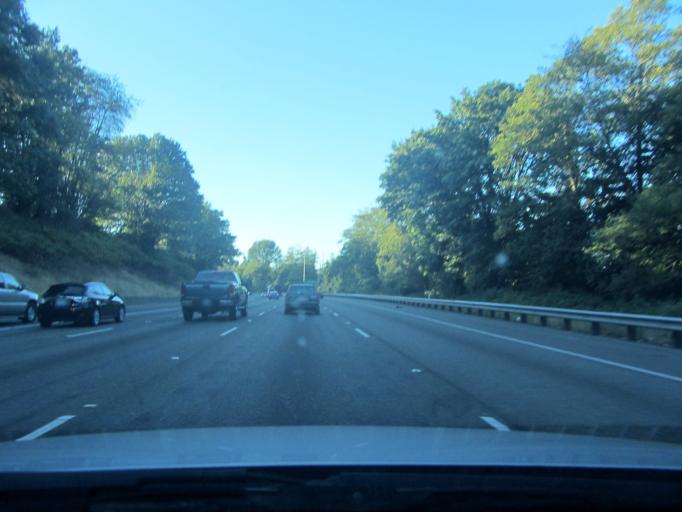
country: US
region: Washington
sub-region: Snohomish County
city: Everett
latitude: 47.9409
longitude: -122.1966
